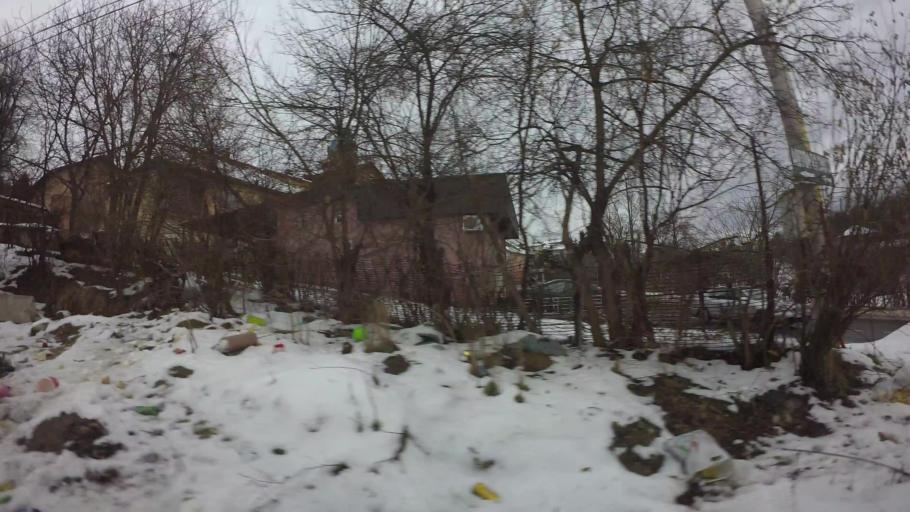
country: BA
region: Federation of Bosnia and Herzegovina
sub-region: Kanton Sarajevo
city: Sarajevo
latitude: 43.8606
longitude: 18.3660
